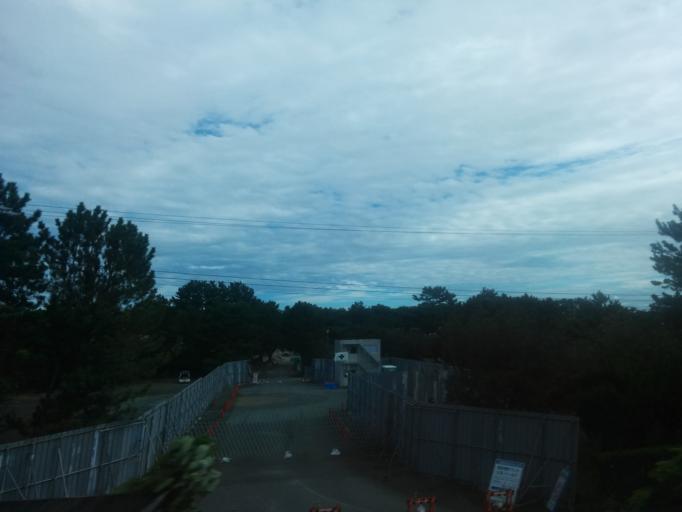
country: JP
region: Shizuoka
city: Kosai-shi
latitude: 34.6936
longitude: 137.5949
